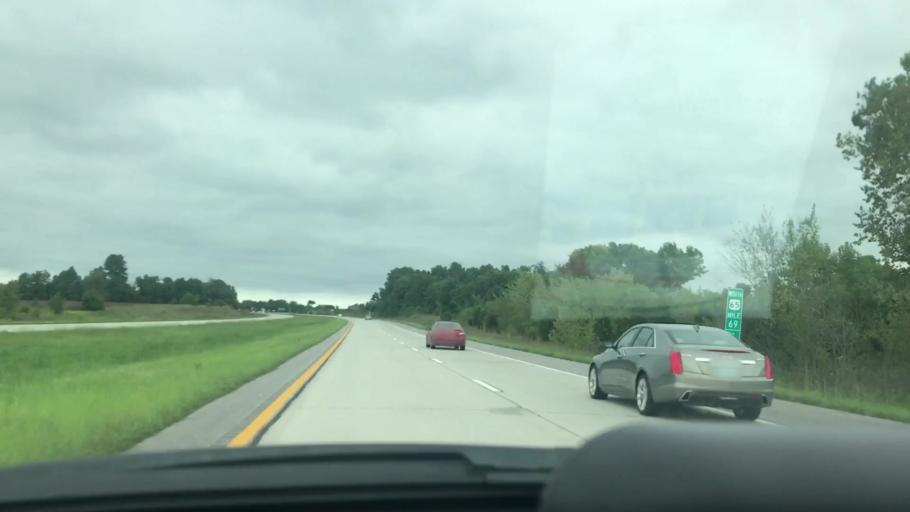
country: US
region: Missouri
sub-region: Greene County
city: Fair Grove
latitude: 37.4511
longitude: -93.1421
